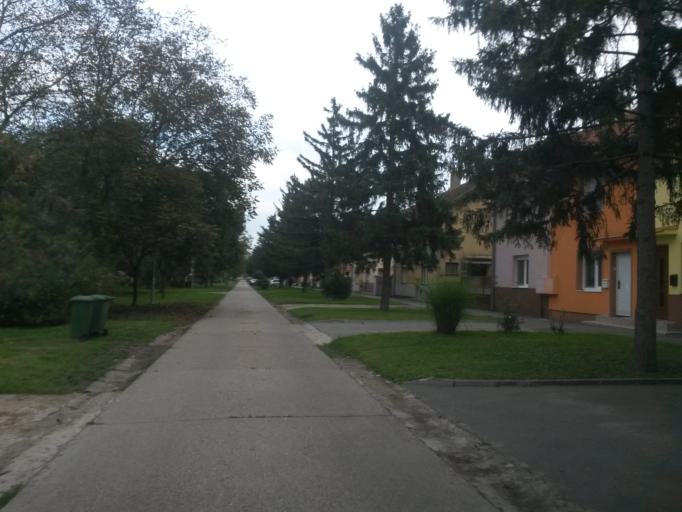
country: HR
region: Osjecko-Baranjska
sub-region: Grad Osijek
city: Osijek
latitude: 45.5465
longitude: 18.6731
